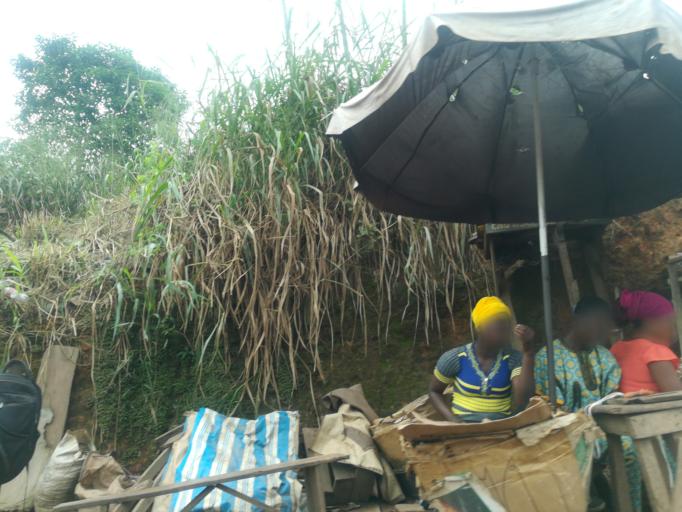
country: NG
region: Oyo
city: Ibadan
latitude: 7.3636
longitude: 3.9269
